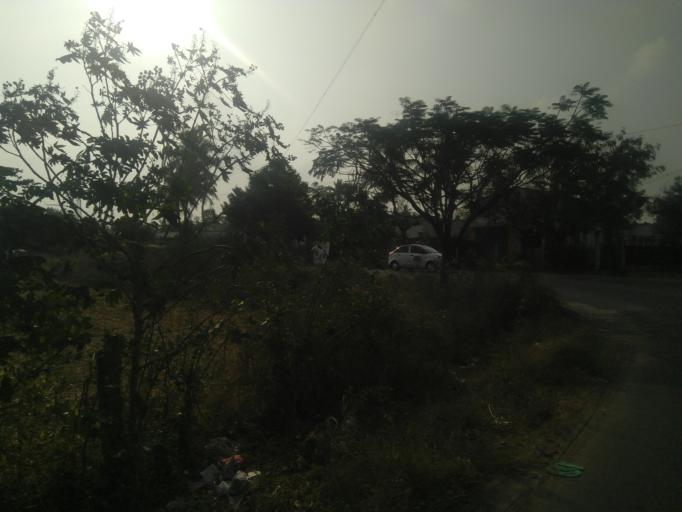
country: IN
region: Tamil Nadu
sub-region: Coimbatore
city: Periyanayakkanpalaiyam
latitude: 11.0786
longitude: 76.9291
